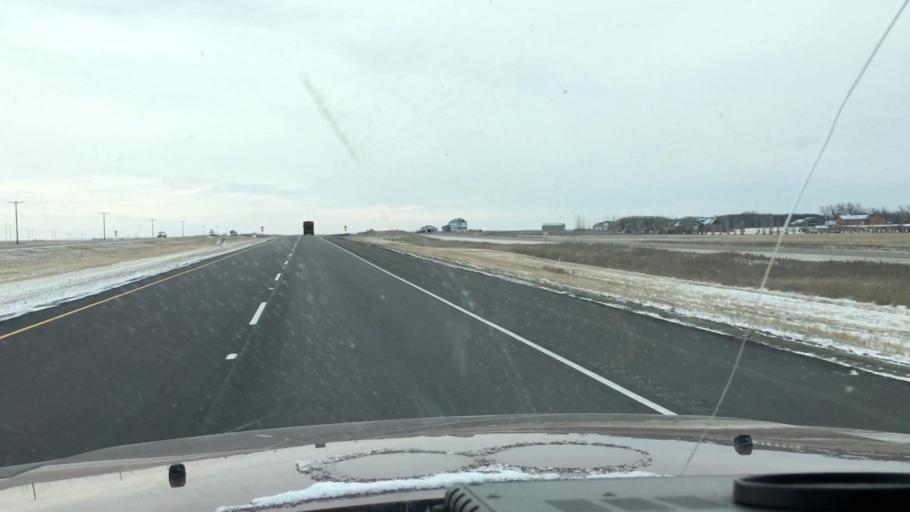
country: CA
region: Saskatchewan
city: Saskatoon
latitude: 51.9326
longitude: -106.5366
